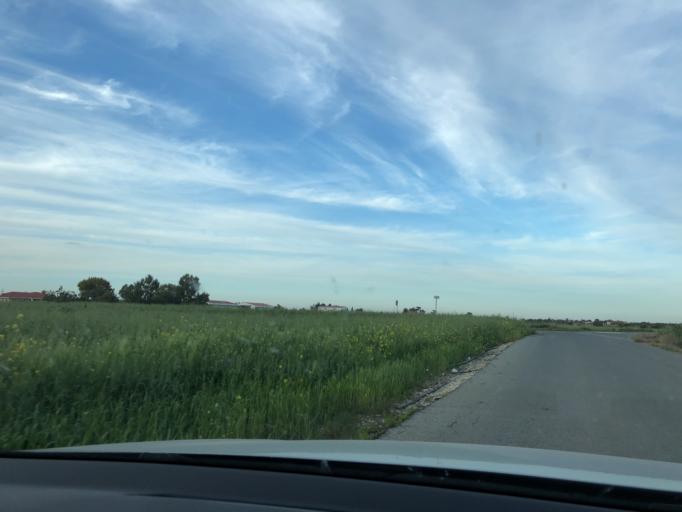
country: CY
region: Larnaka
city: Perivolia
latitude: 34.8301
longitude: 33.5899
